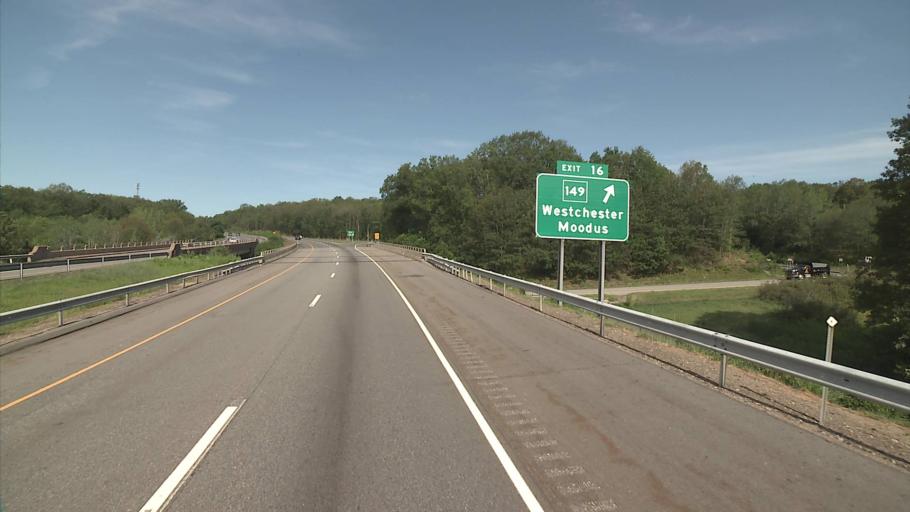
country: US
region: Connecticut
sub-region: New London County
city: Colchester
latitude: 41.5912
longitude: -72.3931
